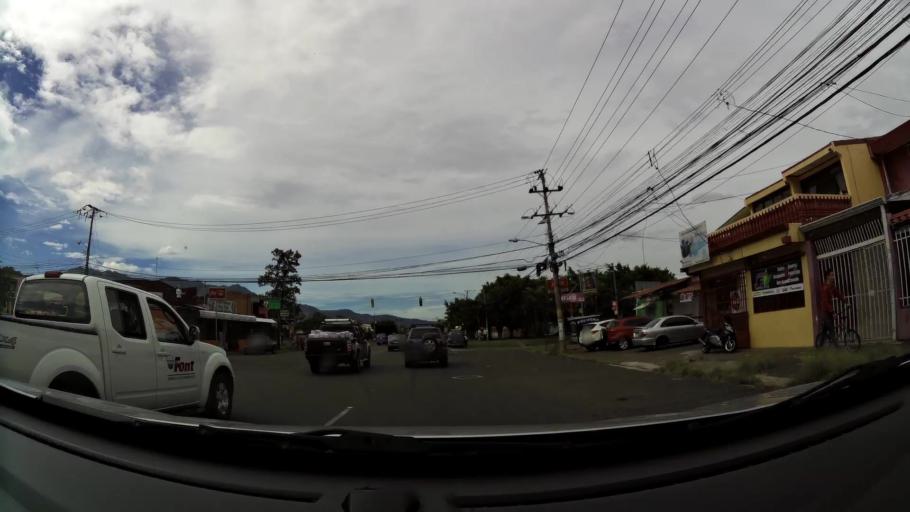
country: CR
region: San Jose
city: Curridabat
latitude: 9.8986
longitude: -84.0537
